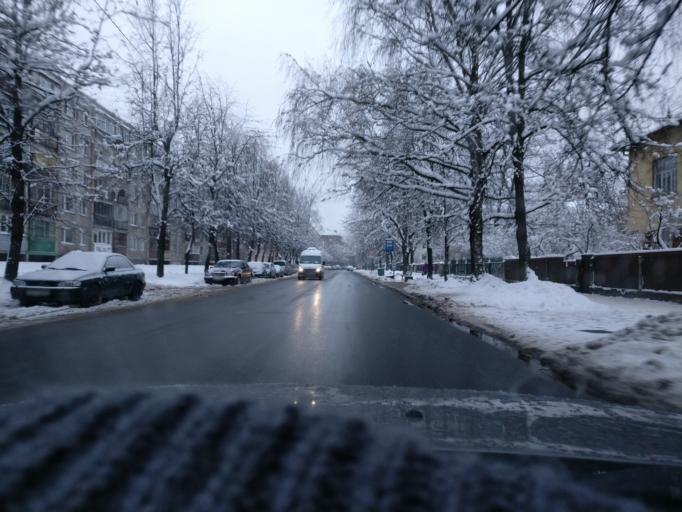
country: LV
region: Marupe
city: Marupe
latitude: 56.9300
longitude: 24.0748
